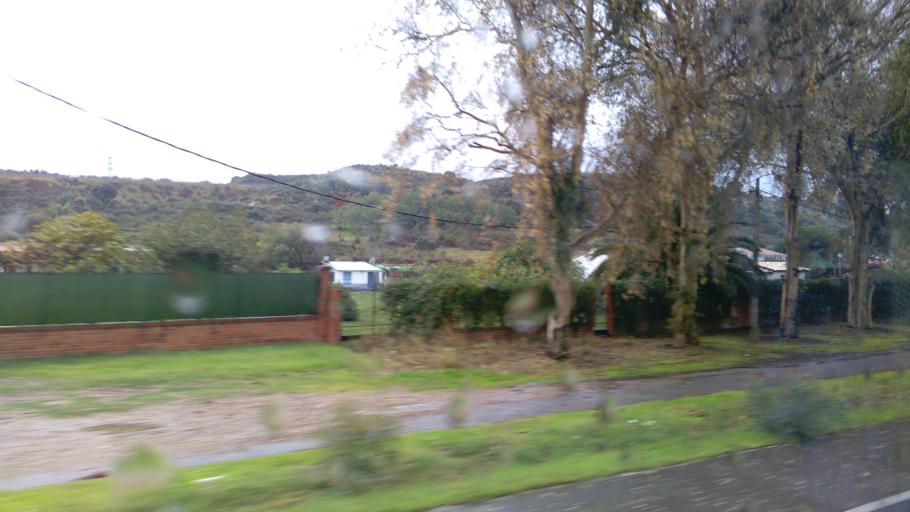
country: ES
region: Extremadura
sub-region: Provincia de Caceres
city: Navalmoral de la Mata
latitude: 39.8914
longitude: -5.5194
